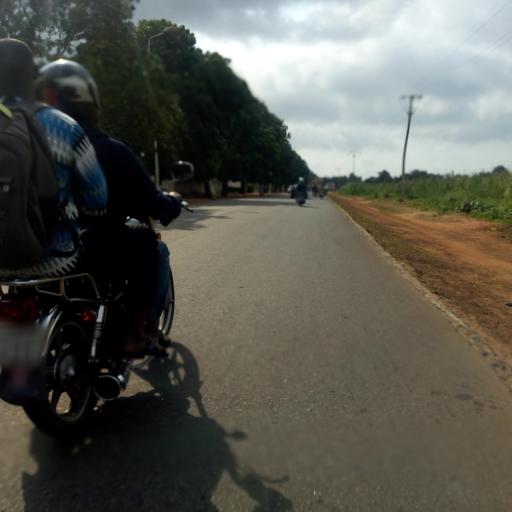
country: TG
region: Maritime
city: Lome
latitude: 6.1913
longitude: 1.2343
